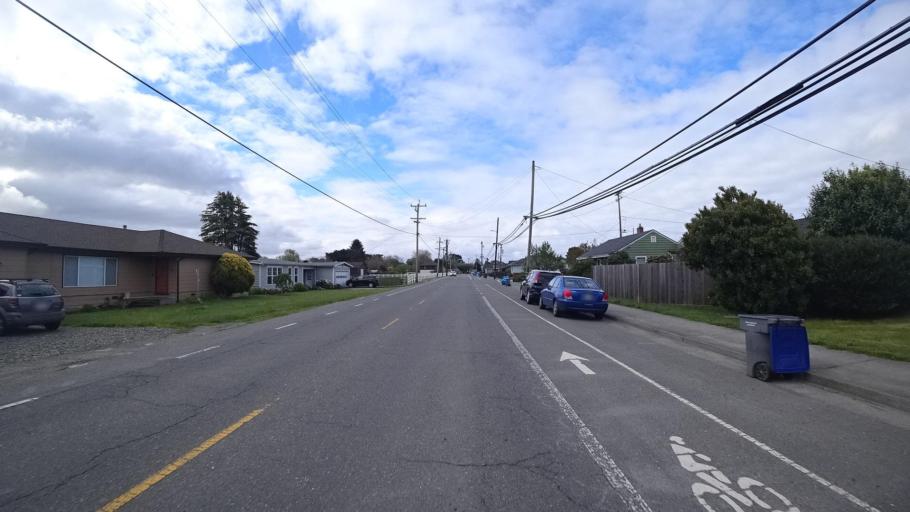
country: US
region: California
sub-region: Humboldt County
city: Arcata
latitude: 40.8887
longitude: -124.0880
